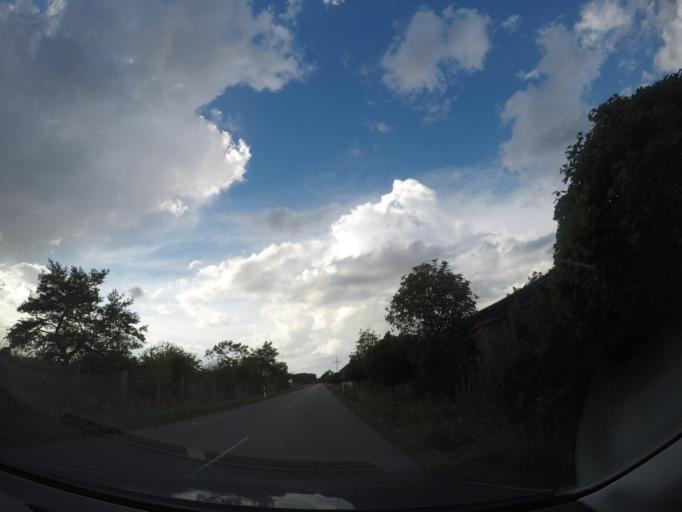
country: DE
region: Saxony-Anhalt
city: Calvorde
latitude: 52.4460
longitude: 11.3038
